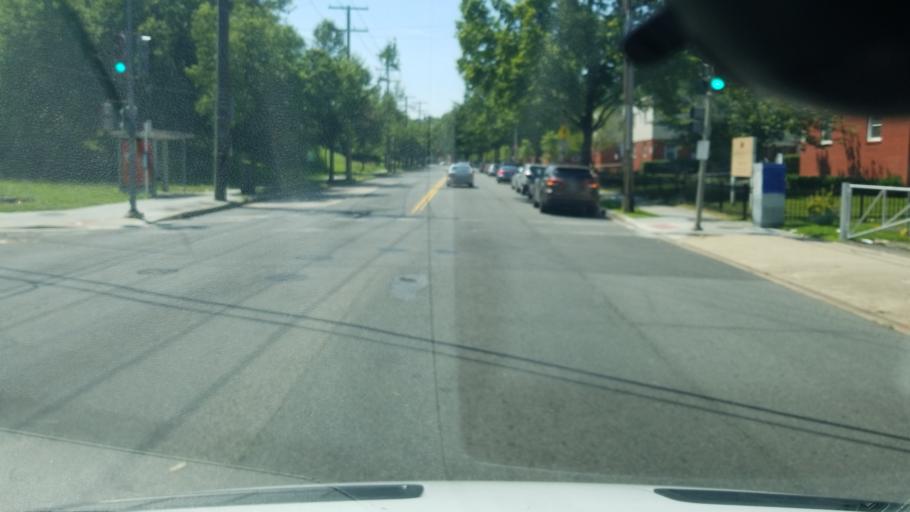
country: US
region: Maryland
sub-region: Prince George's County
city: Capitol Heights
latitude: 38.8860
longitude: -76.9359
